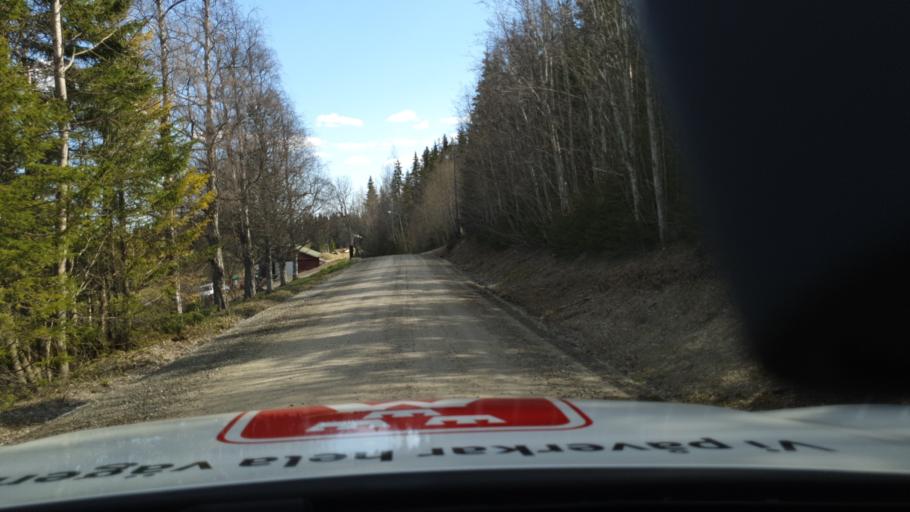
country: SE
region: Jaemtland
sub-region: Bergs Kommun
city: Hoverberg
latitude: 62.9256
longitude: 14.2984
